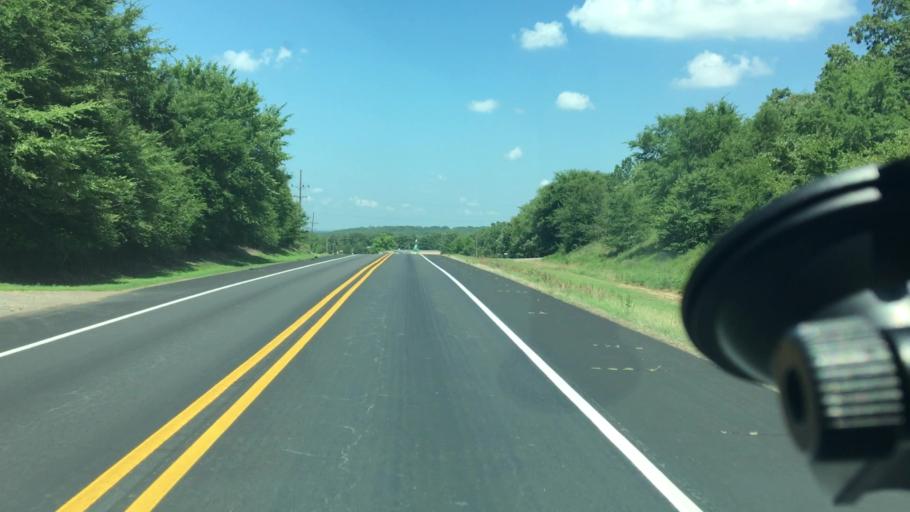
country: US
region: Arkansas
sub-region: Sebastian County
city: Lavaca
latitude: 35.3004
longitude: -94.1592
